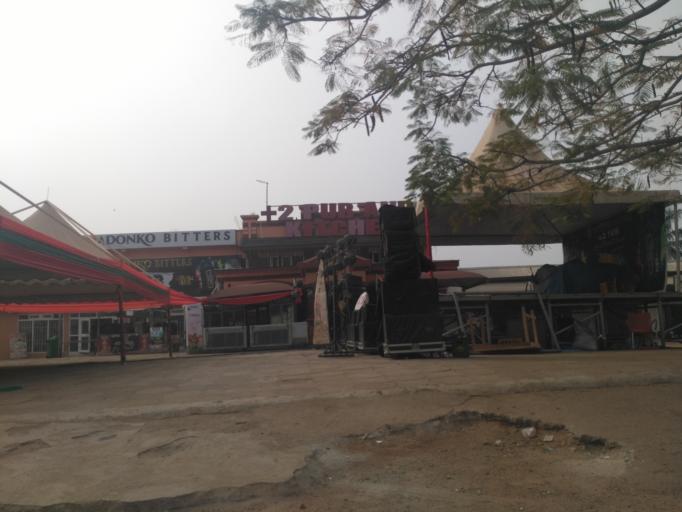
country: GH
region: Ashanti
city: Kumasi
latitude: 6.6693
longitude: -1.6241
